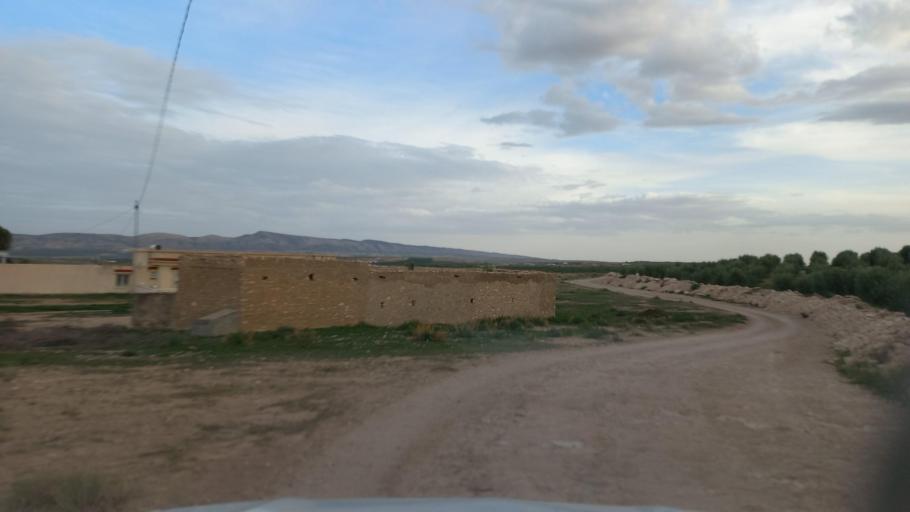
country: TN
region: Al Qasrayn
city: Sbiba
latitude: 35.4321
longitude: 9.0983
